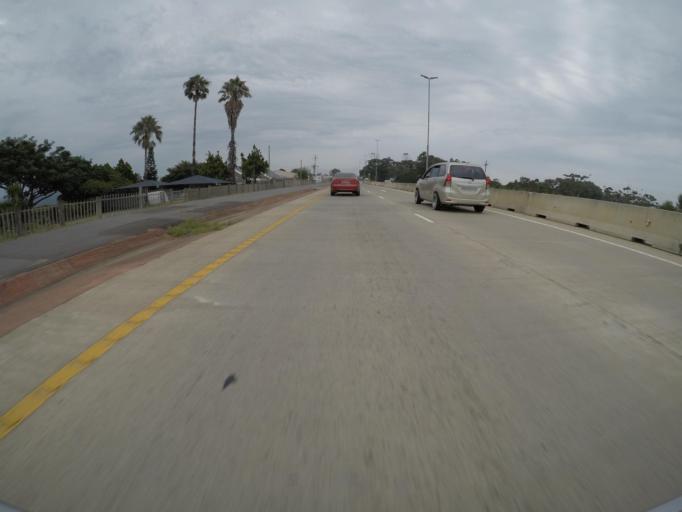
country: ZA
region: Eastern Cape
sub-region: Buffalo City Metropolitan Municipality
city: East London
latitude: -32.9415
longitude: 27.9725
